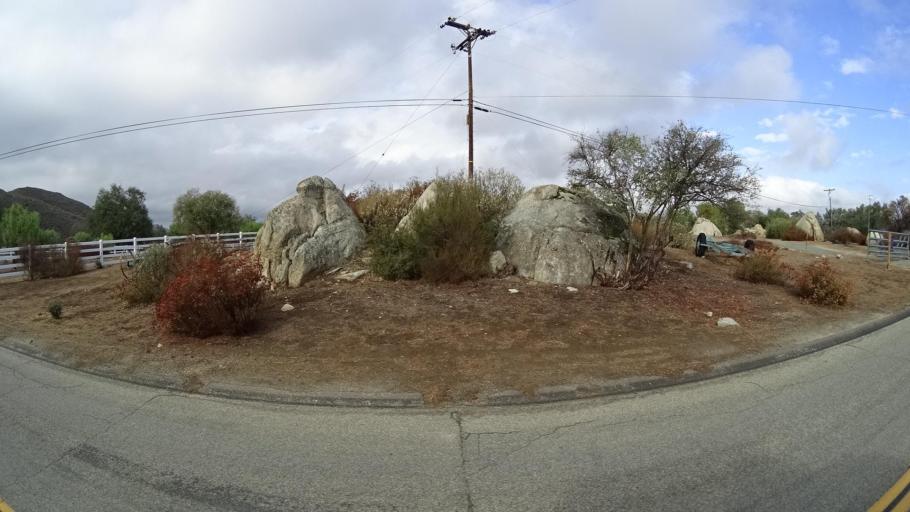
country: MX
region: Baja California
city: Tecate
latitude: 32.6329
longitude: -116.6350
